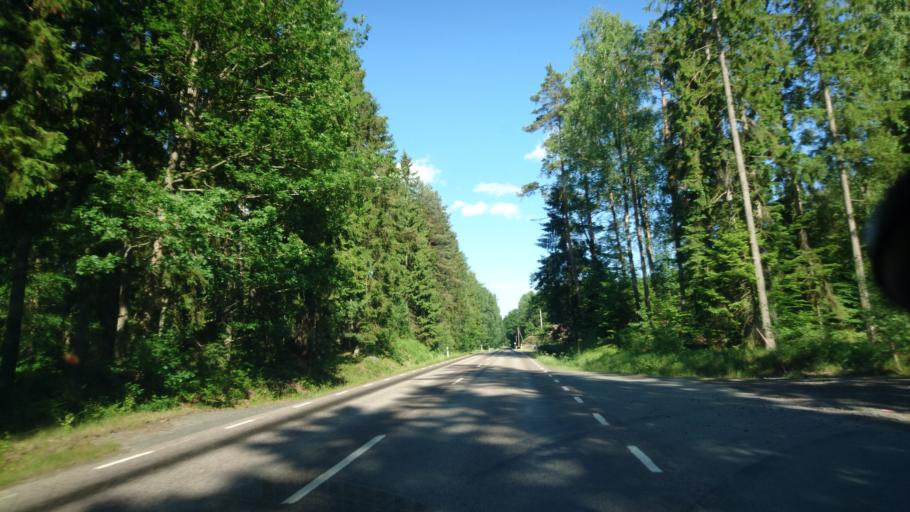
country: SE
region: Skane
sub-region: Osby Kommun
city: Lonsboda
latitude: 56.3910
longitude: 14.3523
